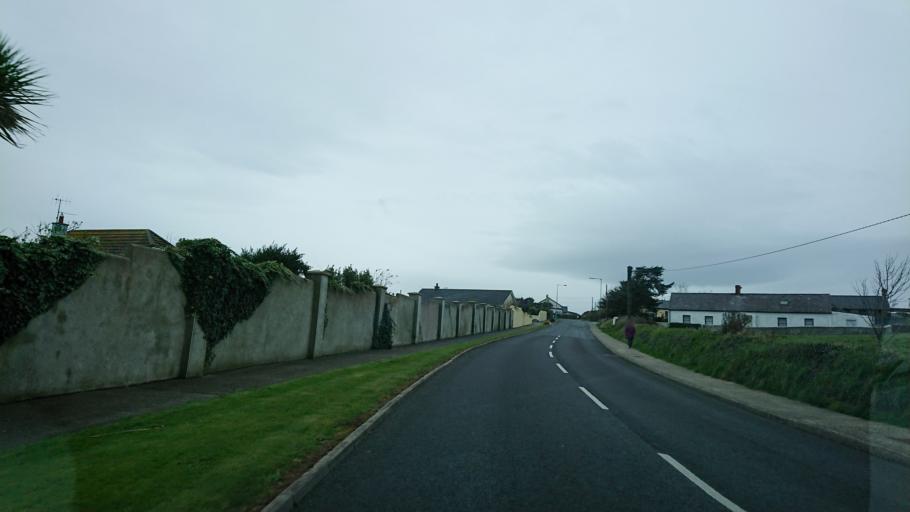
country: IE
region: Munster
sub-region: Waterford
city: Dunmore East
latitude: 52.1464
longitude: -7.0018
